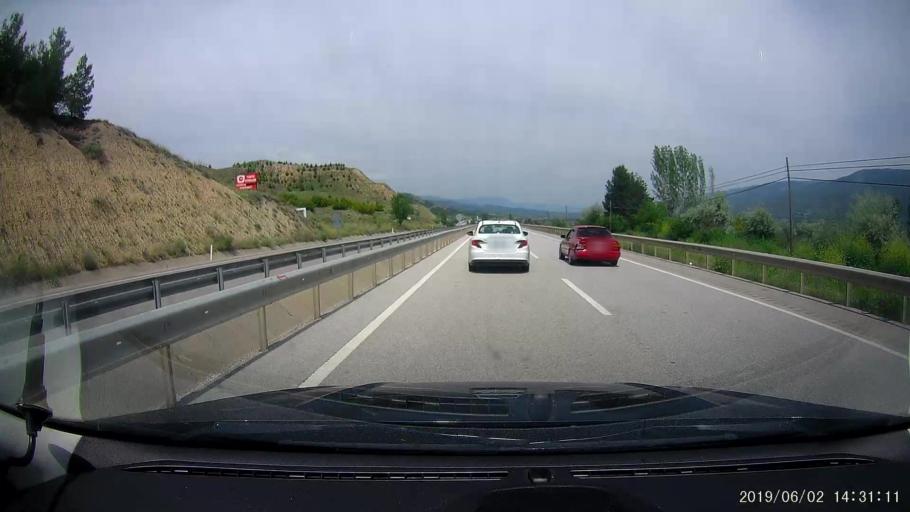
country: TR
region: Kastamonu
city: Tosya
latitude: 41.0158
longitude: 34.1321
